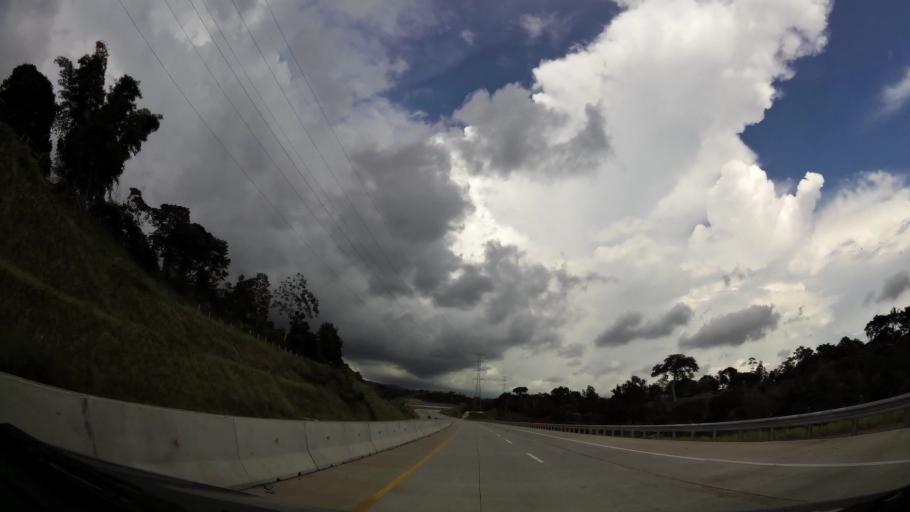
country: PA
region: Panama
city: Tocumen
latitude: 9.1057
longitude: -79.4102
